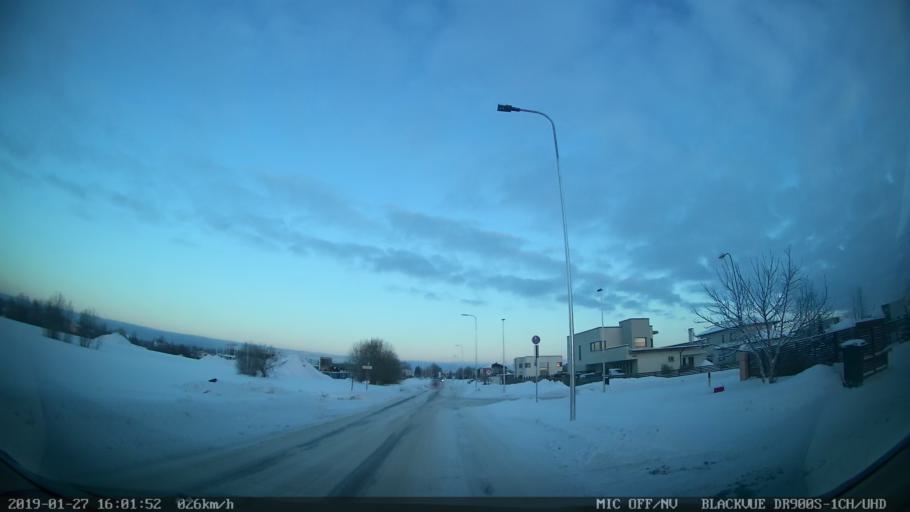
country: EE
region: Harju
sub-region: Tallinna linn
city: Tallinn
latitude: 59.3964
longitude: 24.8023
